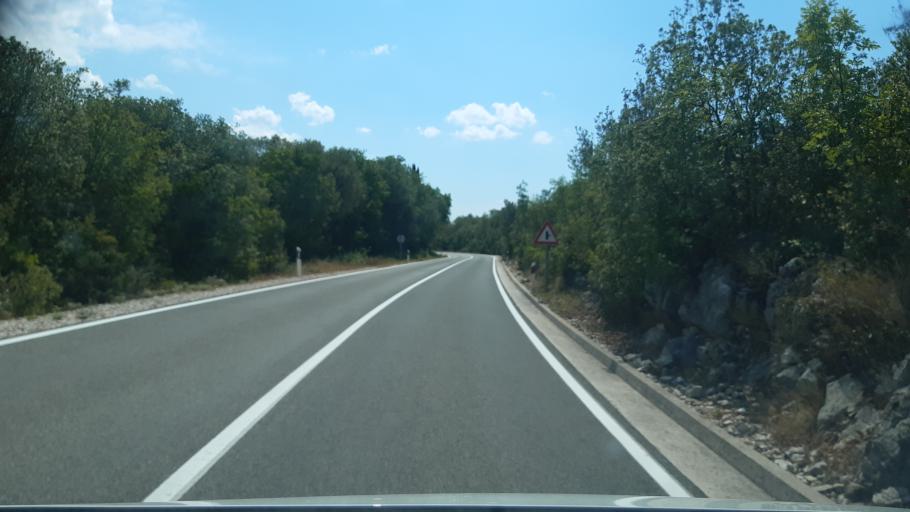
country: HR
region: Dubrovacko-Neretvanska
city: Ston
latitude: 42.8337
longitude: 17.7251
